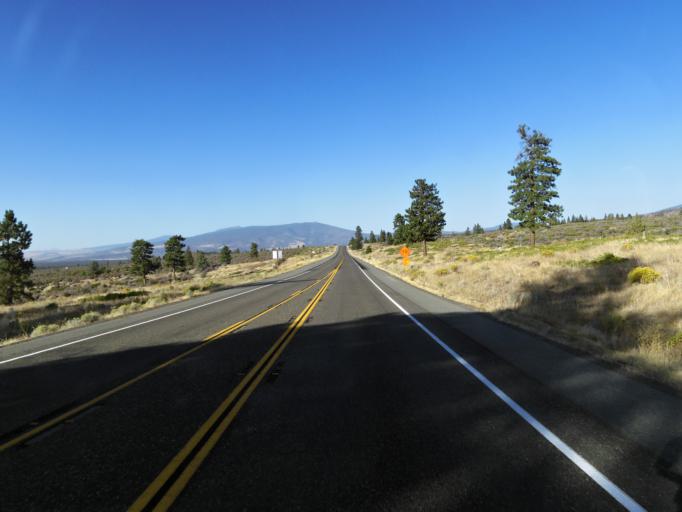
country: US
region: California
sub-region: Siskiyou County
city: Weed
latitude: 41.4862
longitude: -122.3395
